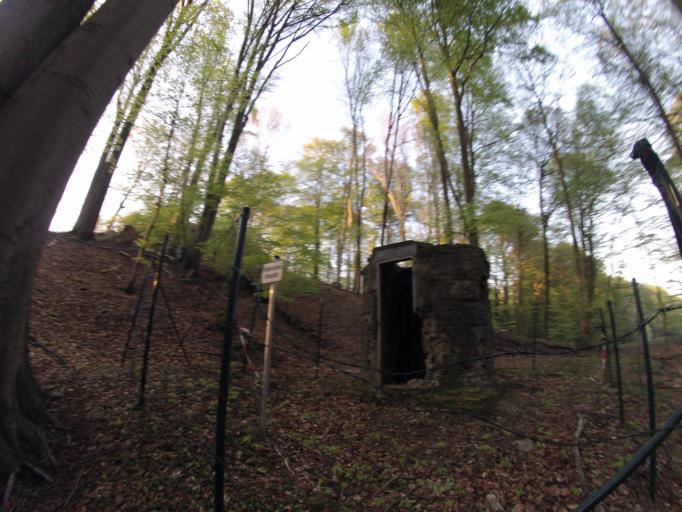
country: DE
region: North Rhine-Westphalia
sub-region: Regierungsbezirk Munster
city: Tecklenburg
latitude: 52.2692
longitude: 7.8257
